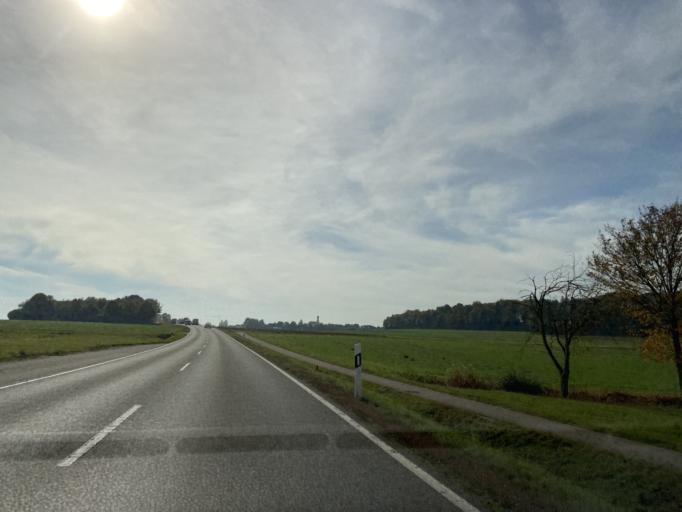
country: DE
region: Baden-Wuerttemberg
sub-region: Tuebingen Region
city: Inzigkofen
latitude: 48.0531
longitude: 9.1405
